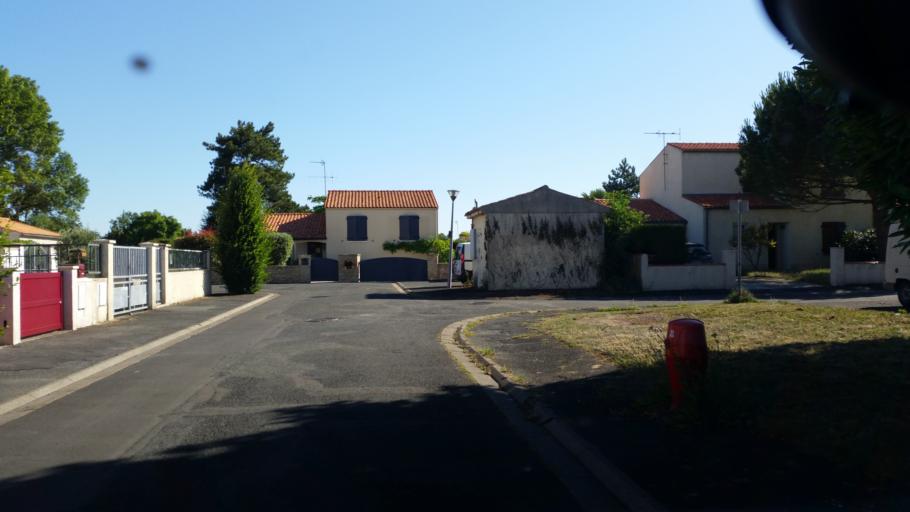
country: FR
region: Poitou-Charentes
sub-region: Departement de la Charente-Maritime
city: Marans
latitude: 46.3037
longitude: -0.9874
